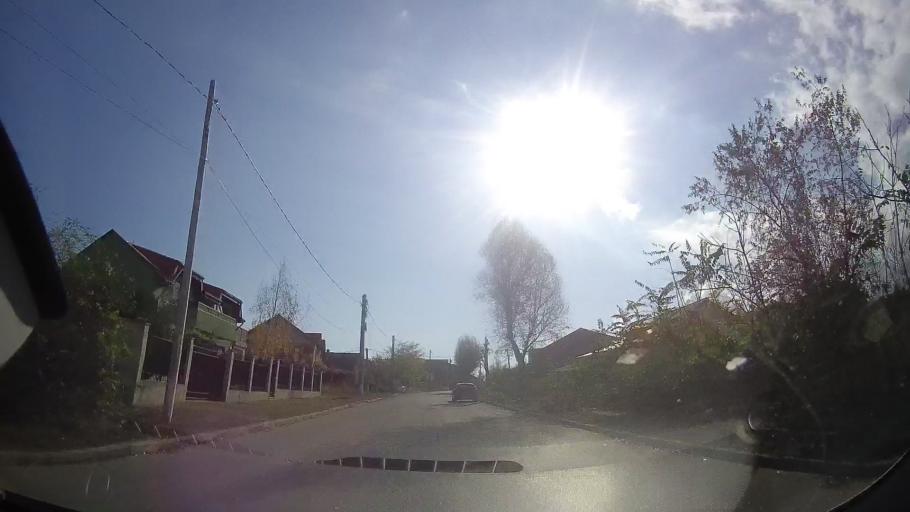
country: RO
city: Eforie Sud
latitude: 44.0172
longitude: 28.6471
